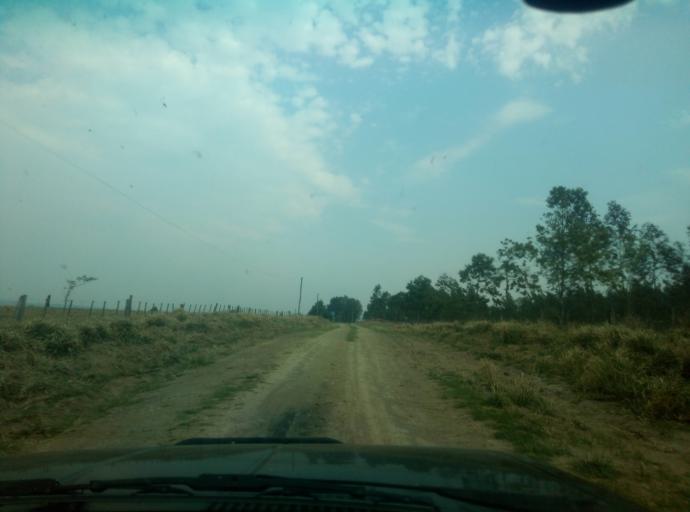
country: PY
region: Caaguazu
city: San Joaquin
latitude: -25.1103
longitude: -56.1275
